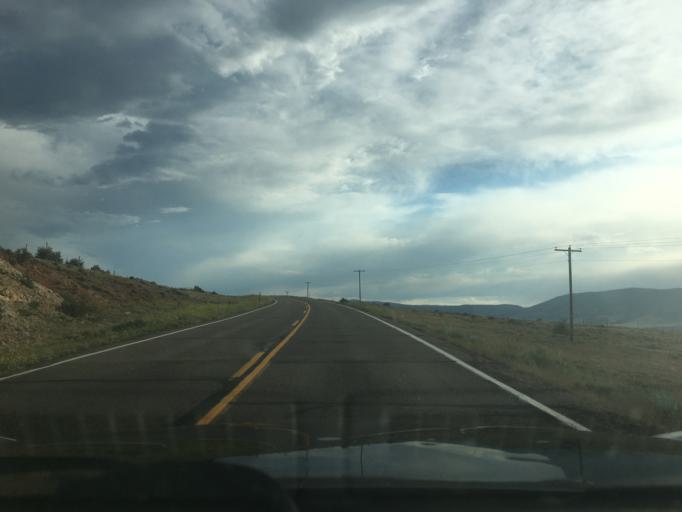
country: US
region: Wyoming
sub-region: Albany County
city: Laramie
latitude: 41.2793
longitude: -106.0648
